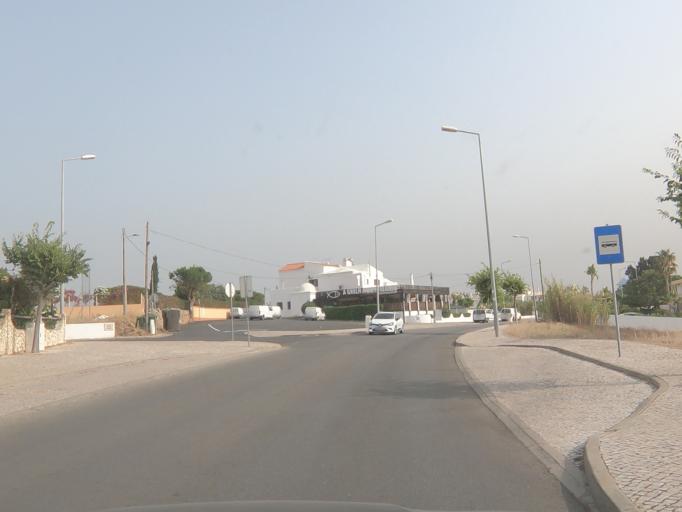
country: PT
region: Faro
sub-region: Albufeira
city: Guia
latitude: 37.0866
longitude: -8.3095
